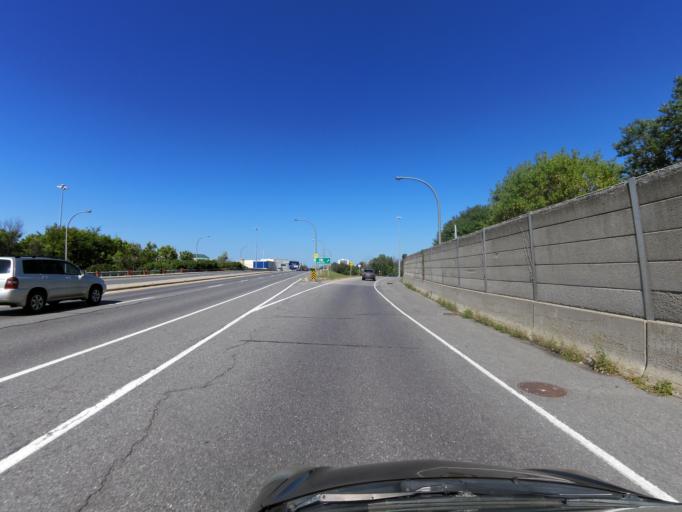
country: CA
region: Ontario
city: Bells Corners
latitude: 45.3439
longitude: -75.8066
